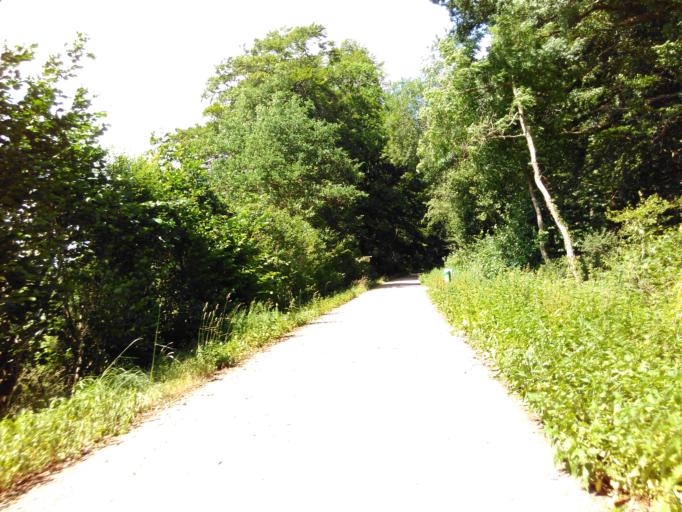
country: LU
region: Luxembourg
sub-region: Canton de Capellen
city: Clemency
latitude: 49.6087
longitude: 5.8770
